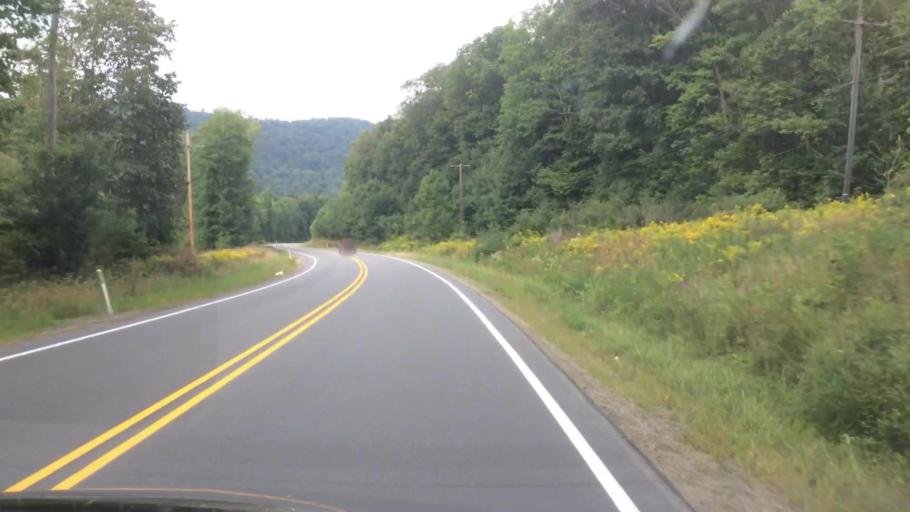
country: US
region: Pennsylvania
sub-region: McKean County
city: Bradford
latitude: 41.8869
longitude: -78.5948
